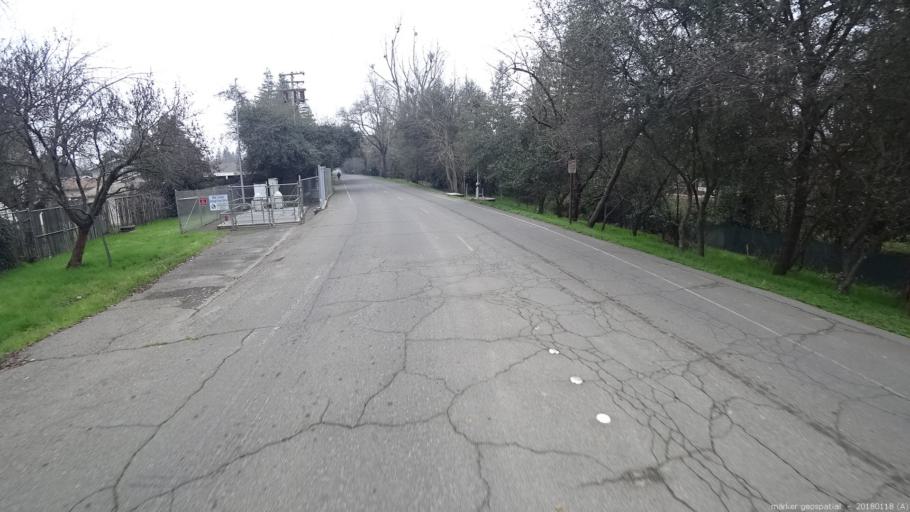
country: US
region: California
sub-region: Sacramento County
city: Rancho Cordova
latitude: 38.5885
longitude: -121.3244
